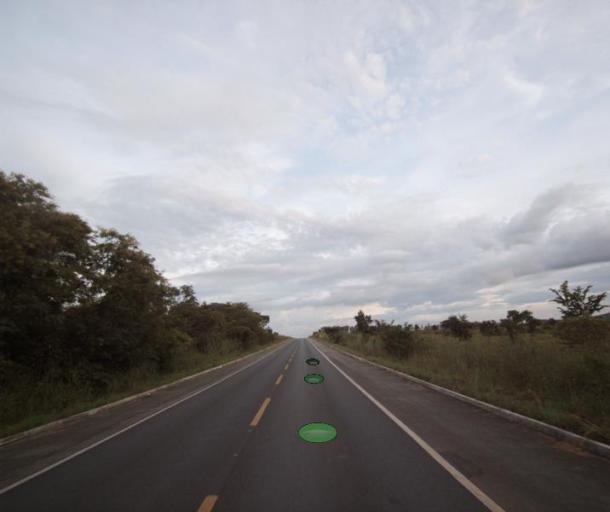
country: BR
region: Goias
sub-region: Barro Alto
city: Barro Alto
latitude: -15.2000
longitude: -48.7021
